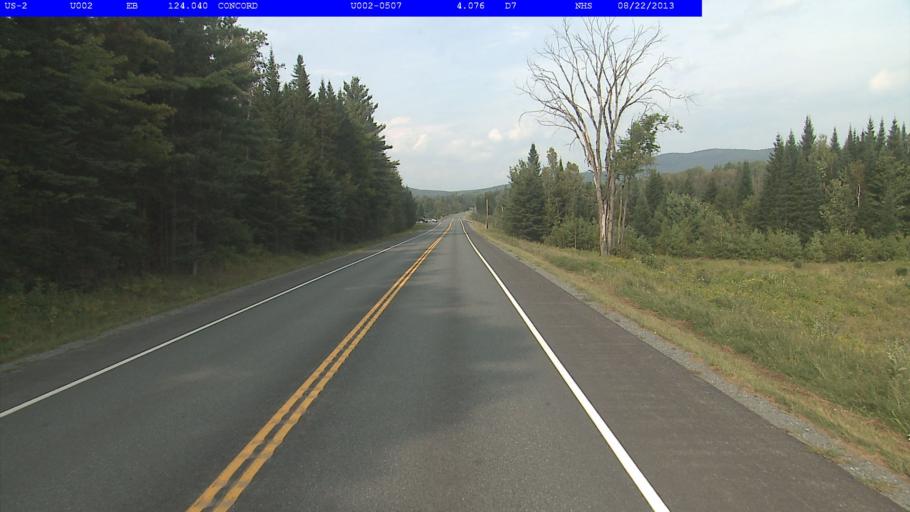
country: US
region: Vermont
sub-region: Caledonia County
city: St Johnsbury
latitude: 44.4519
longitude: -71.8713
